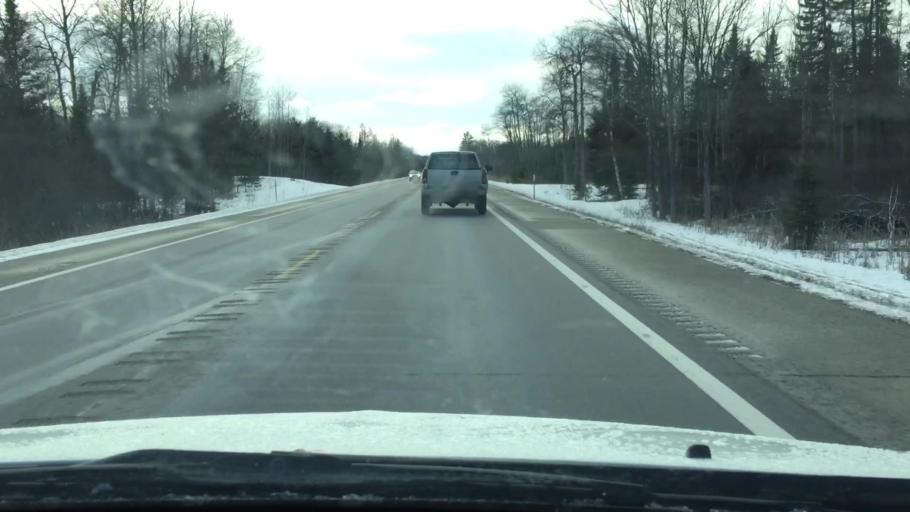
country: US
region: Michigan
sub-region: Kalkaska County
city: Kalkaska
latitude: 44.6598
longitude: -85.2541
